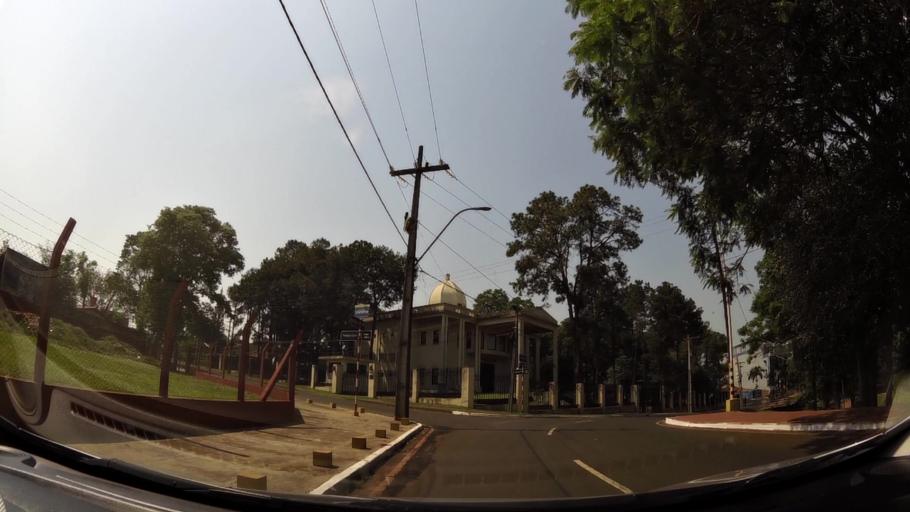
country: PY
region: Alto Parana
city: Ciudad del Este
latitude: -25.5180
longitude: -54.6173
